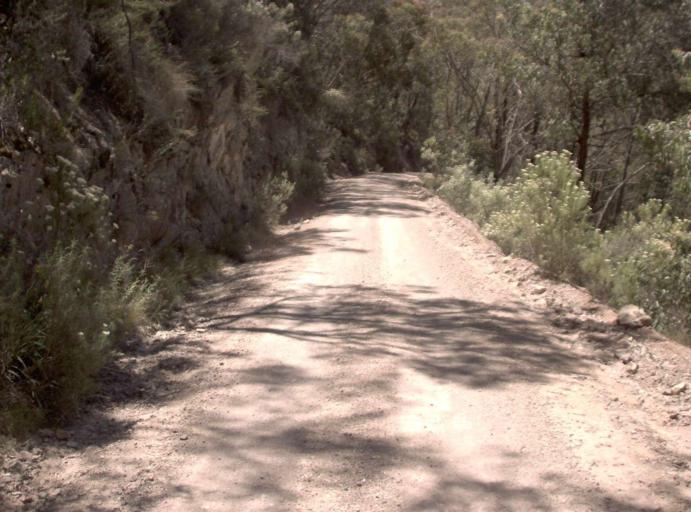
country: AU
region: New South Wales
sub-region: Snowy River
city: Jindabyne
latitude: -37.0862
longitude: 148.3308
